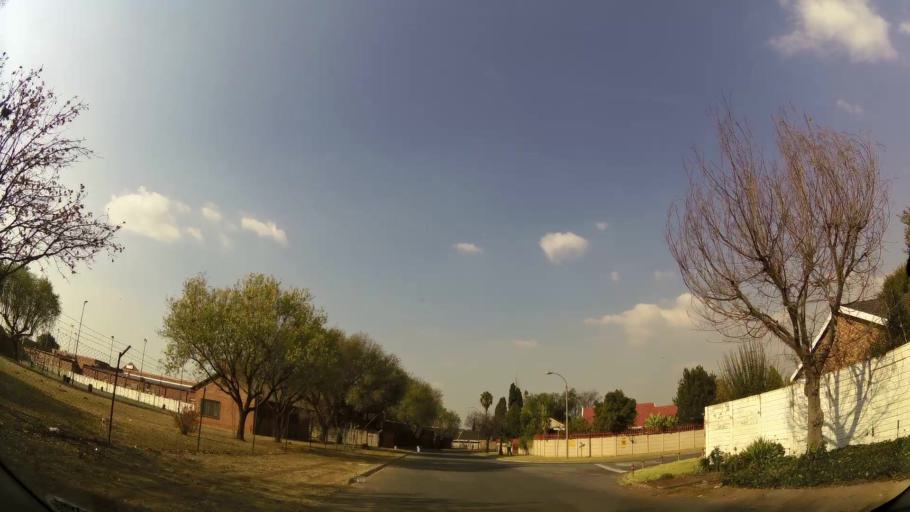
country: ZA
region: Gauteng
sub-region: Ekurhuleni Metropolitan Municipality
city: Benoni
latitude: -26.1608
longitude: 28.2793
